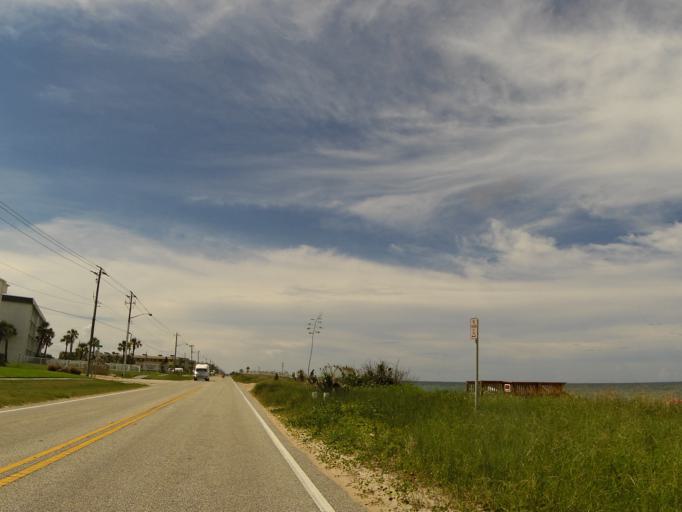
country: US
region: Florida
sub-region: Volusia County
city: Ormond-by-the-Sea
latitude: 29.3419
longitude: -81.0629
